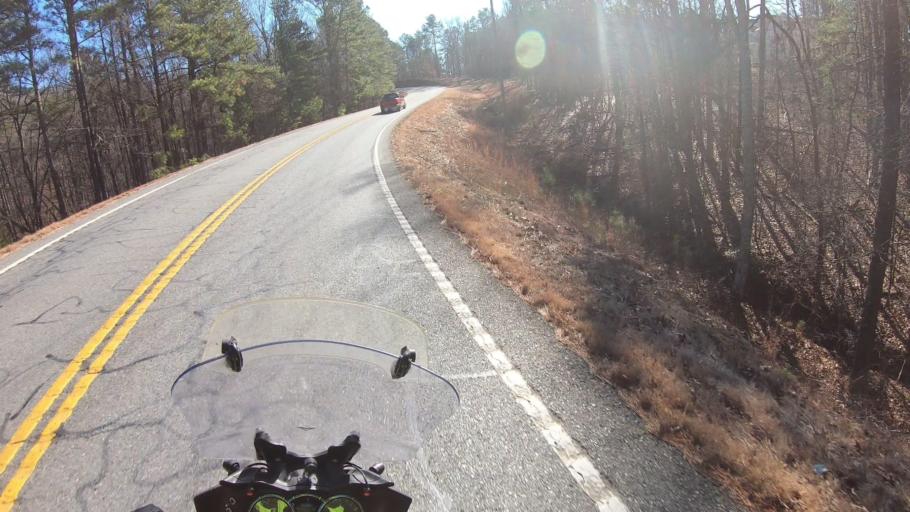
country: US
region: Georgia
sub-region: Gilmer County
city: Ellijay
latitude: 34.5843
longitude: -84.6102
